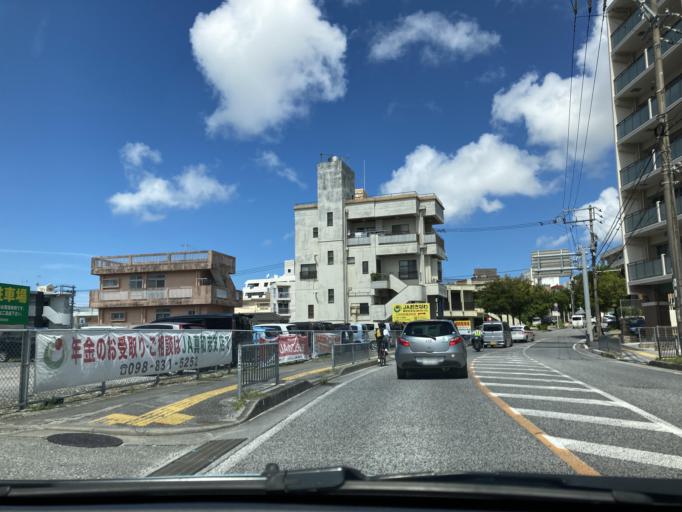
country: JP
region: Okinawa
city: Naha-shi
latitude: 26.2065
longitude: 127.6990
